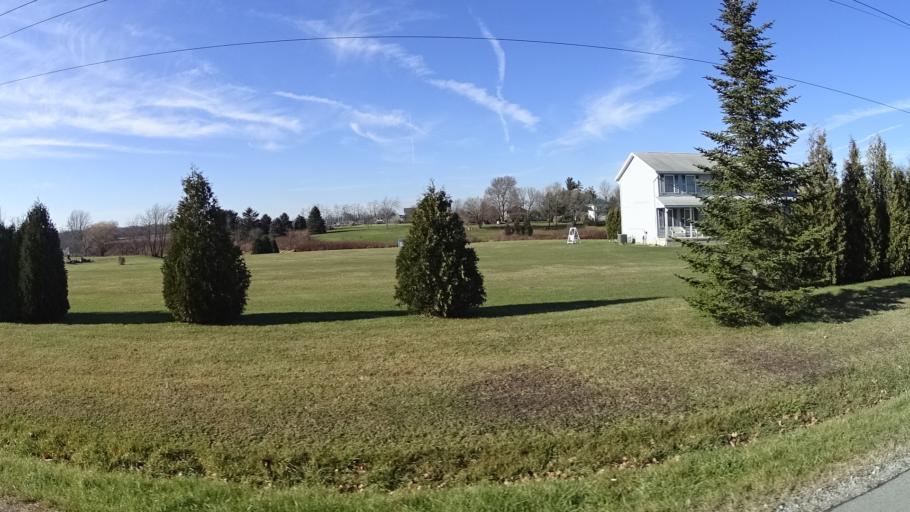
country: US
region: Ohio
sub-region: Huron County
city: New London
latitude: 41.0732
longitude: -82.3042
